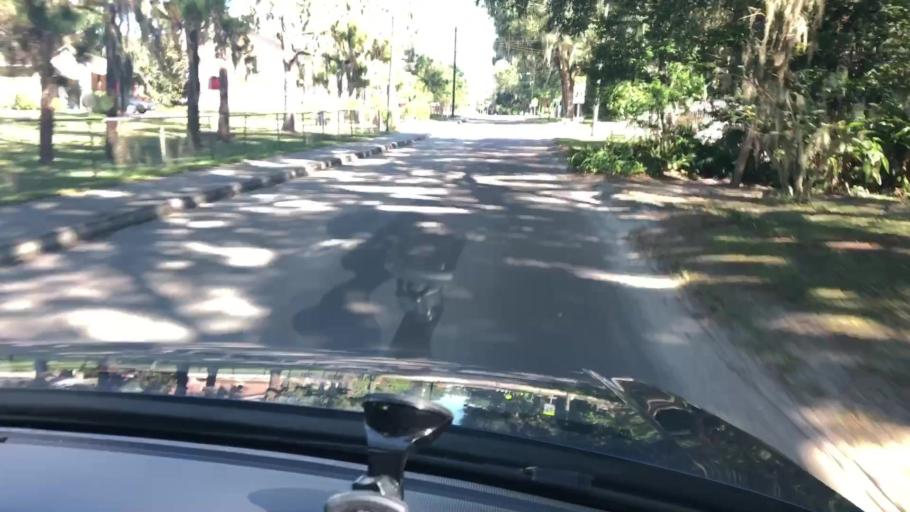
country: US
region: Florida
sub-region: Polk County
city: Kathleen
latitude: 28.1244
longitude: -82.0212
